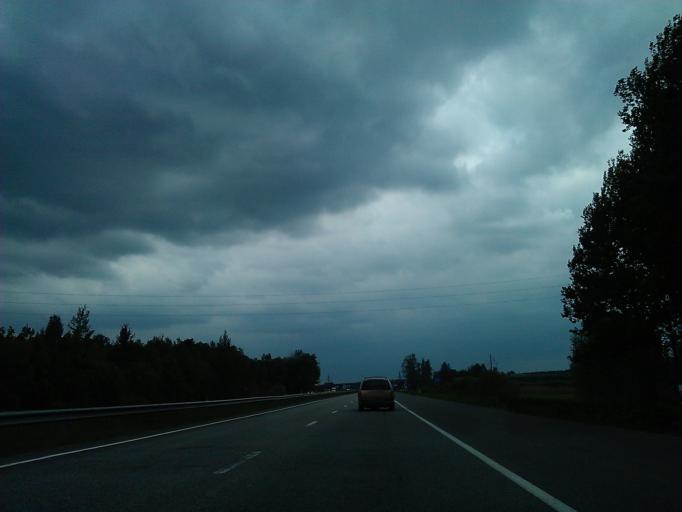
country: LV
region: Marupe
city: Marupe
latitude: 56.8390
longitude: 24.0475
